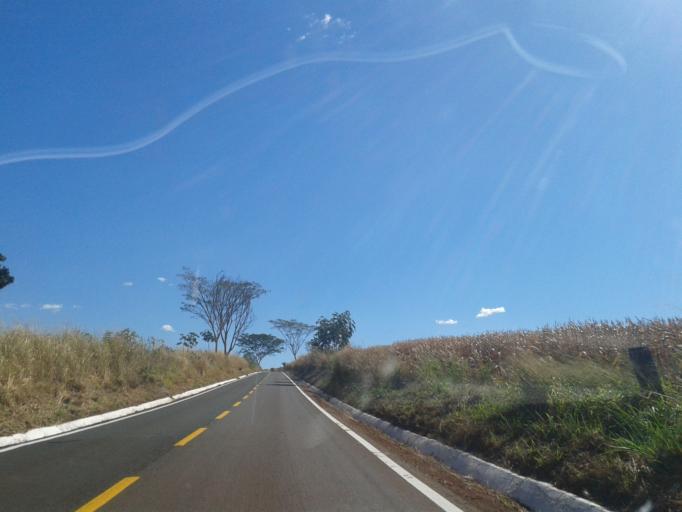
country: BR
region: Minas Gerais
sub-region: Capinopolis
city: Capinopolis
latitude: -18.6917
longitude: -49.4591
